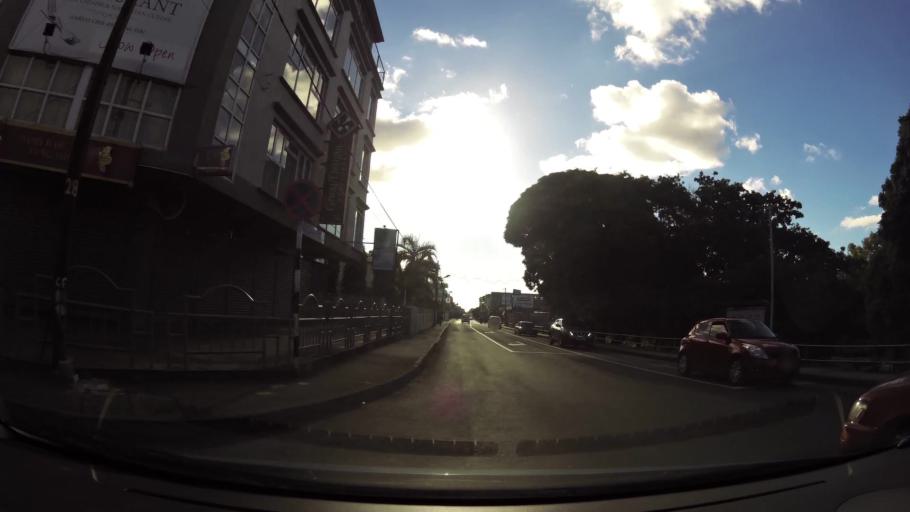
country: MU
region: Plaines Wilhems
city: Ebene
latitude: -20.2470
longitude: 57.4805
